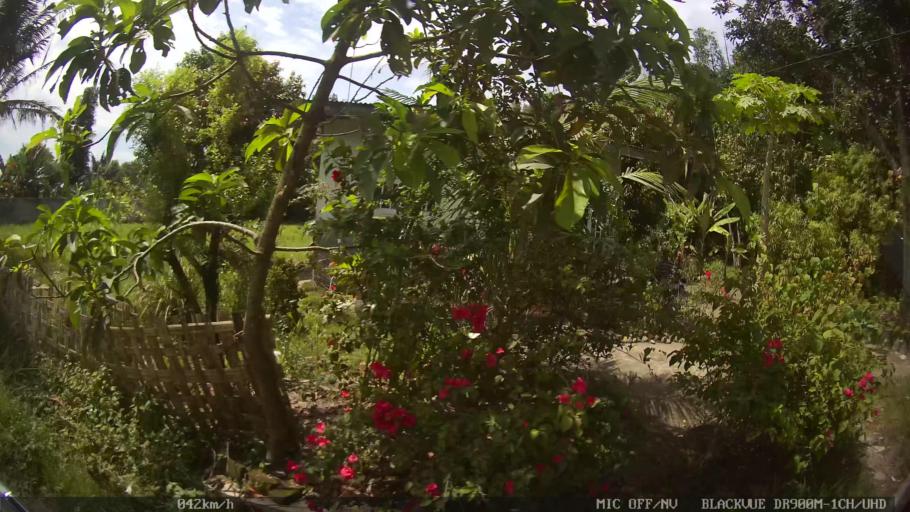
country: ID
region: North Sumatra
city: Percut
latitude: 3.6058
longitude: 98.8569
